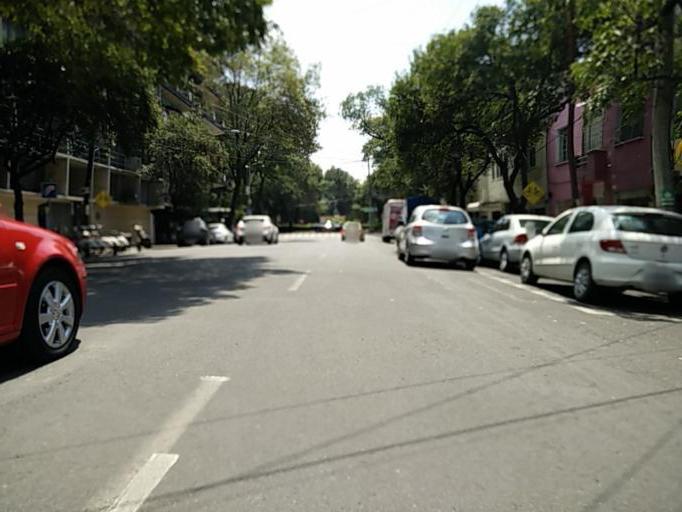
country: MX
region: Mexico City
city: Benito Juarez
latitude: 19.4224
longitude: -99.1607
